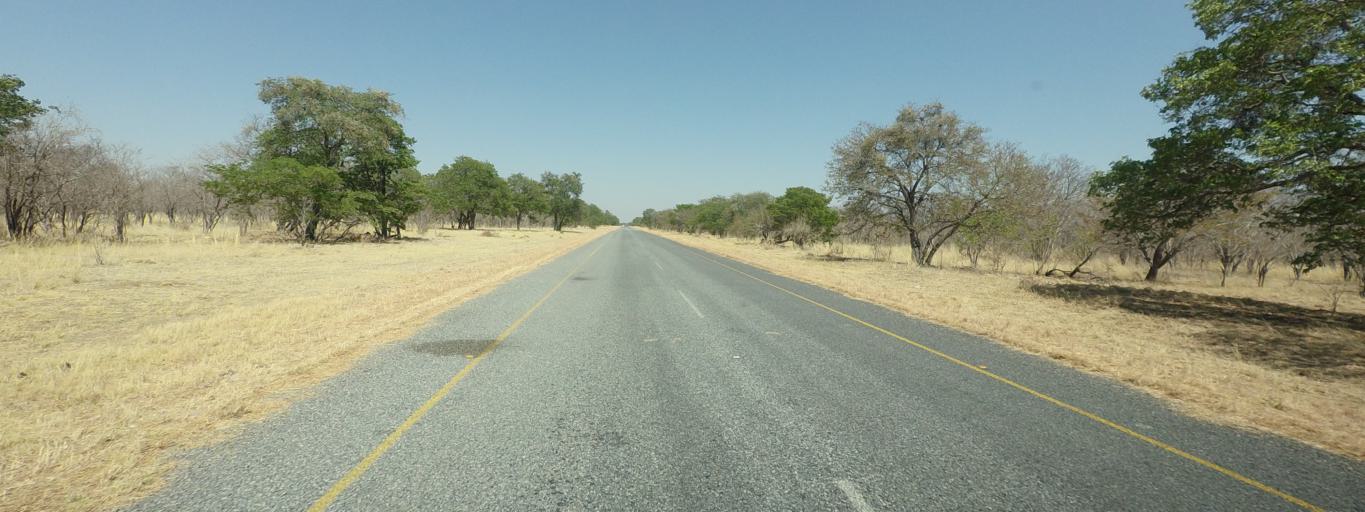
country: BW
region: North West
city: Kasane
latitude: -17.9218
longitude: 24.9506
